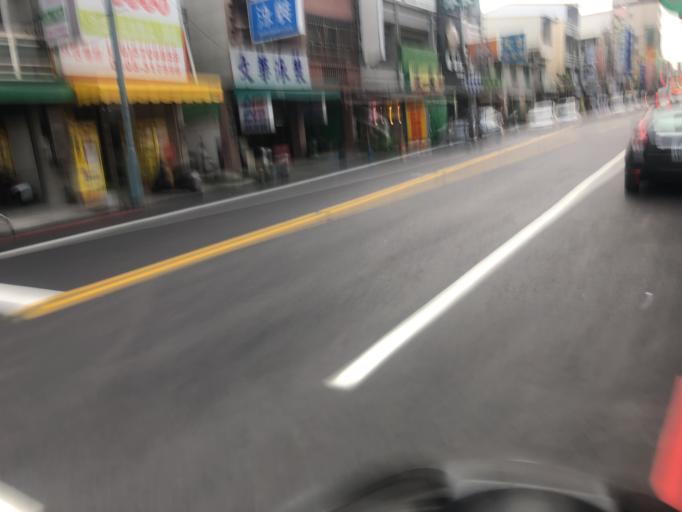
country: TW
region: Taiwan
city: Xinying
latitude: 23.1838
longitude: 120.2533
